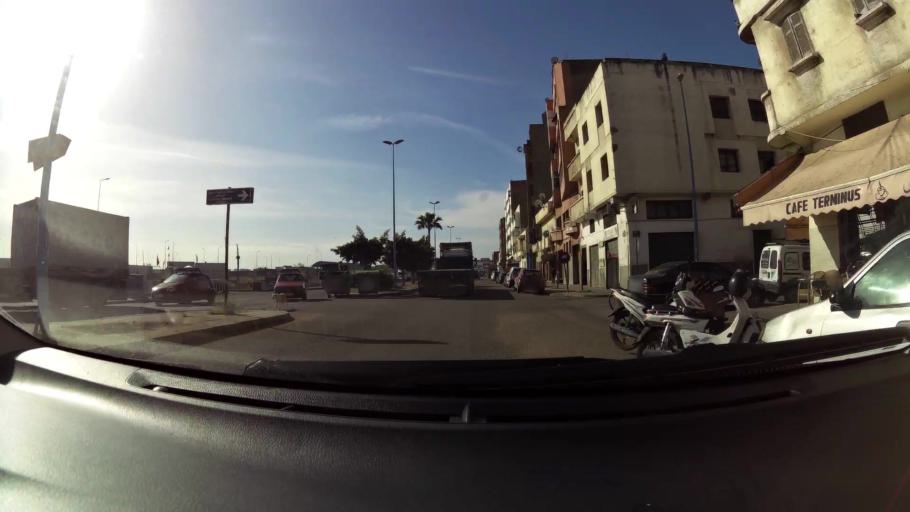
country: MA
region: Grand Casablanca
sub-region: Casablanca
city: Casablanca
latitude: 33.6006
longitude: -7.5781
